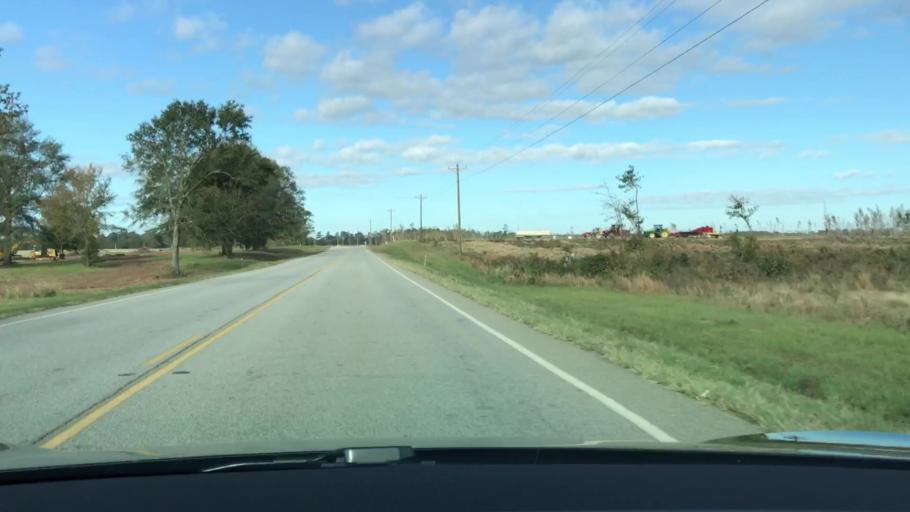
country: US
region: Georgia
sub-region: Jefferson County
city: Wrens
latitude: 33.1151
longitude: -82.4350
